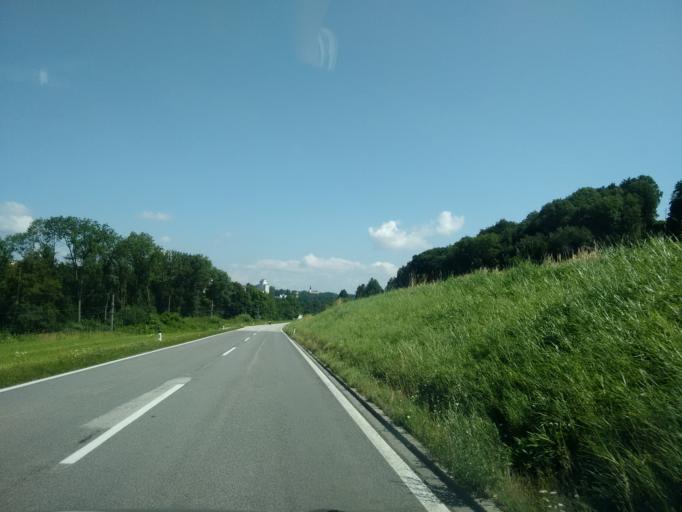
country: AT
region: Upper Austria
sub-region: Politischer Bezirk Kirchdorf an der Krems
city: Kremsmunster
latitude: 48.0418
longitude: 14.1267
